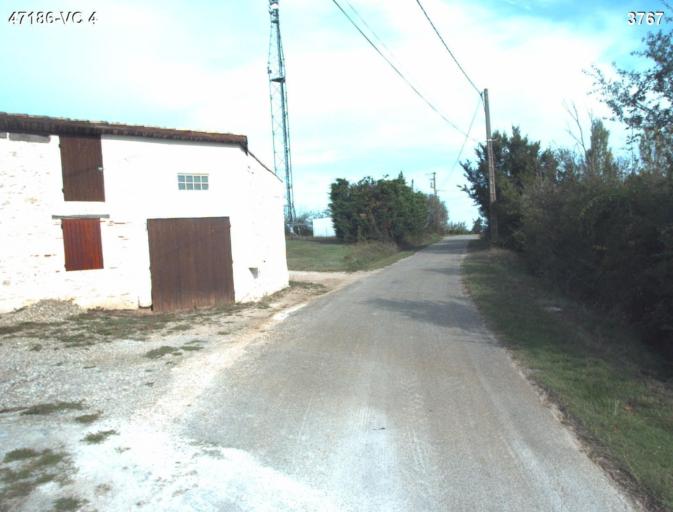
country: FR
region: Aquitaine
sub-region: Departement du Lot-et-Garonne
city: Sainte-Colombe-en-Bruilhois
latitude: 44.1979
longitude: 0.4459
